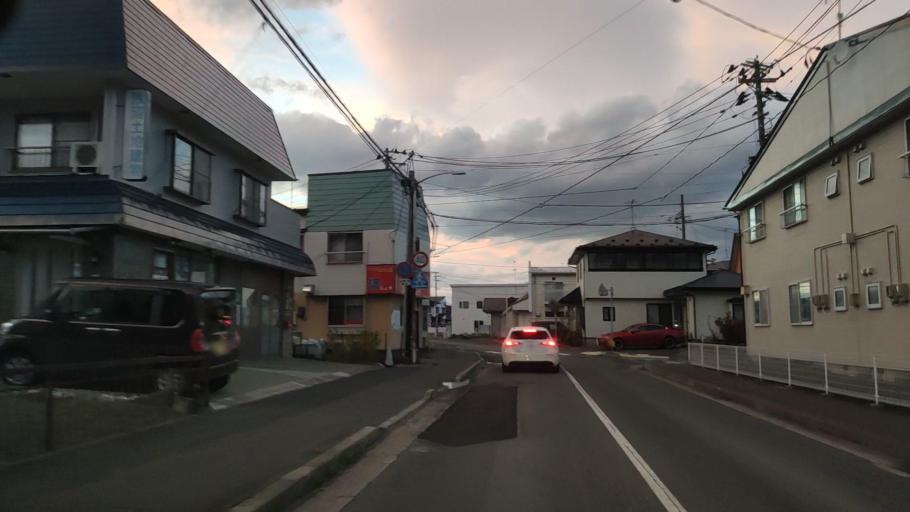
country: JP
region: Iwate
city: Morioka-shi
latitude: 39.7143
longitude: 141.1102
